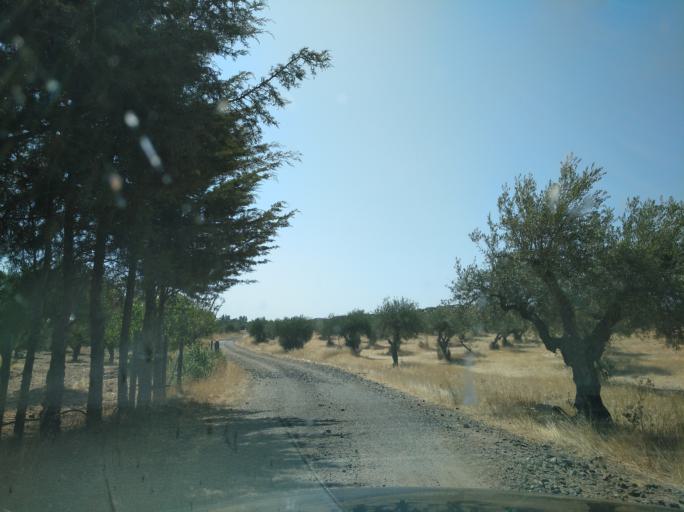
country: PT
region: Portalegre
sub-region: Campo Maior
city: Campo Maior
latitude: 39.0710
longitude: -7.0171
